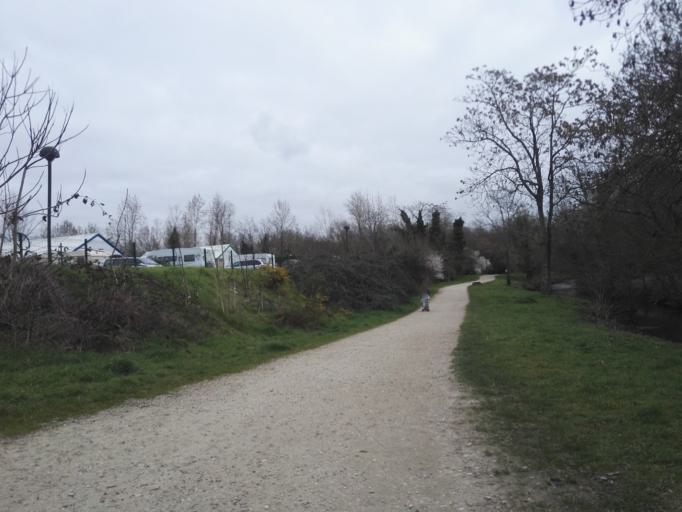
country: FR
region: Aquitaine
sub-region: Departement de la Gironde
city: Villenave-d'Ornon
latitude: 44.7887
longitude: -0.5632
